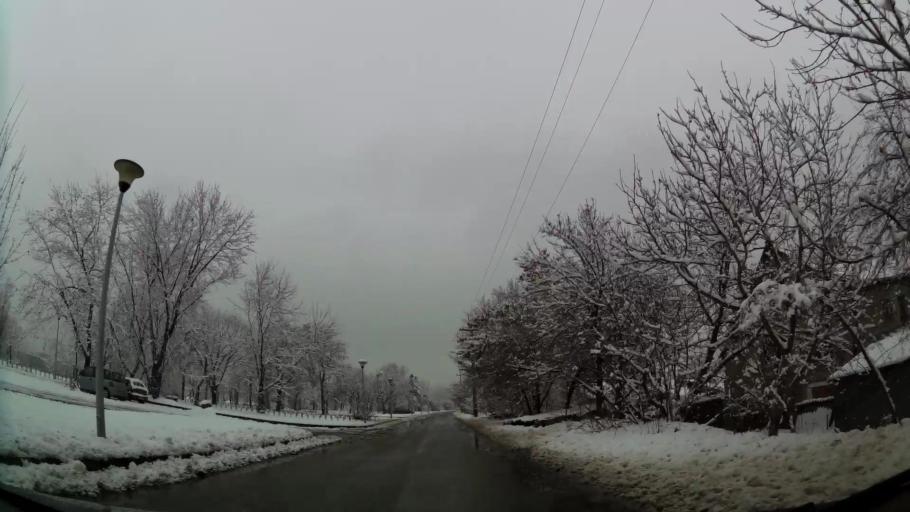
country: RS
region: Central Serbia
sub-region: Belgrade
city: Novi Beograd
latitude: 44.8085
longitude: 20.4428
